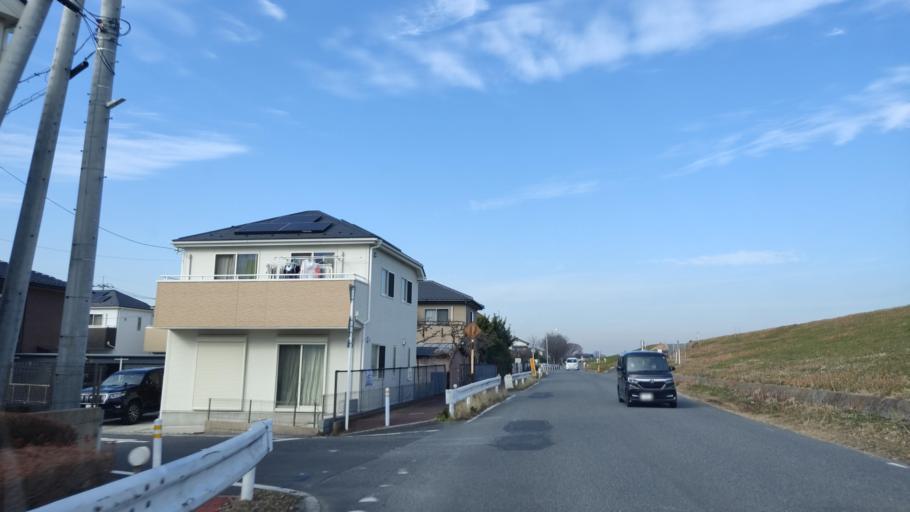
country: JP
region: Chiba
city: Matsudo
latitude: 35.8188
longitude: 139.8877
